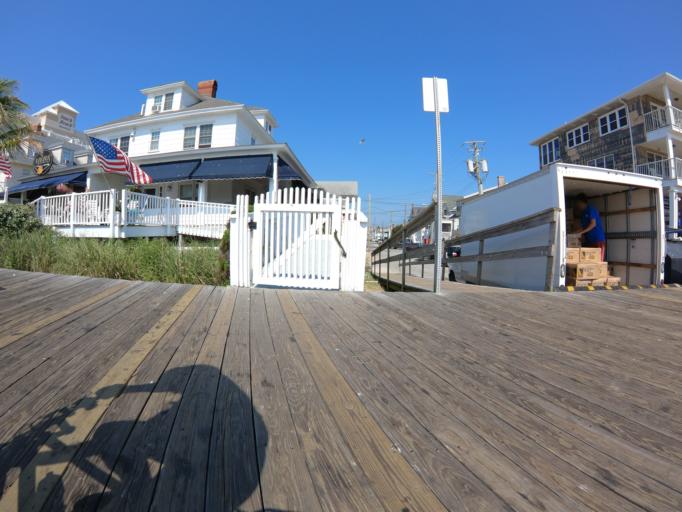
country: US
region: Maryland
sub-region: Worcester County
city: Ocean City
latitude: 38.3386
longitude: -75.0811
